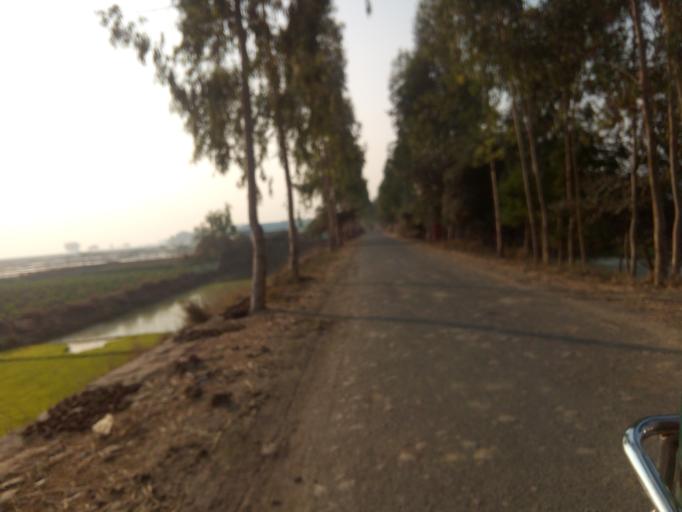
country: BD
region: Rajshahi
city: Bogra
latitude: 24.4773
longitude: 89.2640
